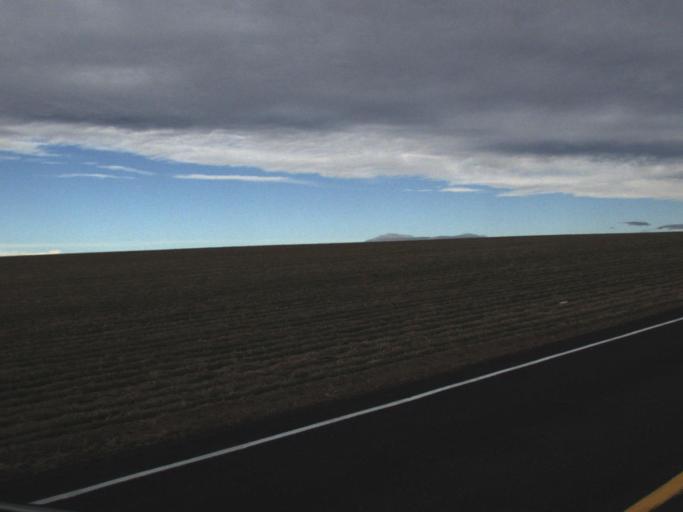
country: US
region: Washington
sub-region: Okanogan County
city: Coulee Dam
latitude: 47.6209
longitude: -118.7206
